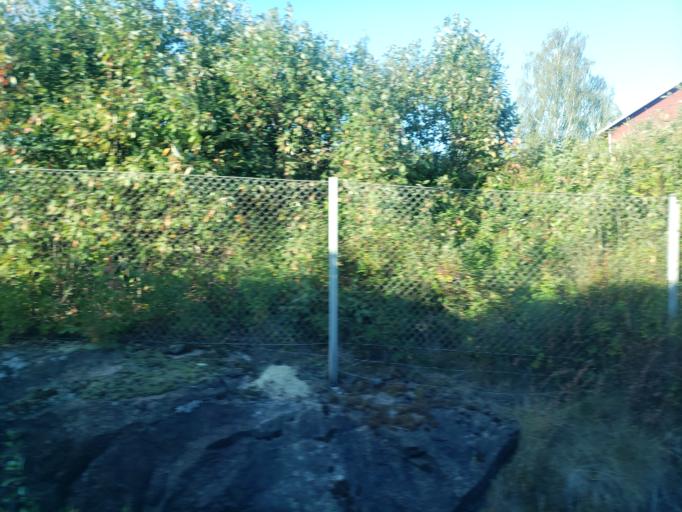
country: FI
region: South Karelia
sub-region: Lappeenranta
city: Lappeenranta
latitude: 60.8685
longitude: 28.2859
